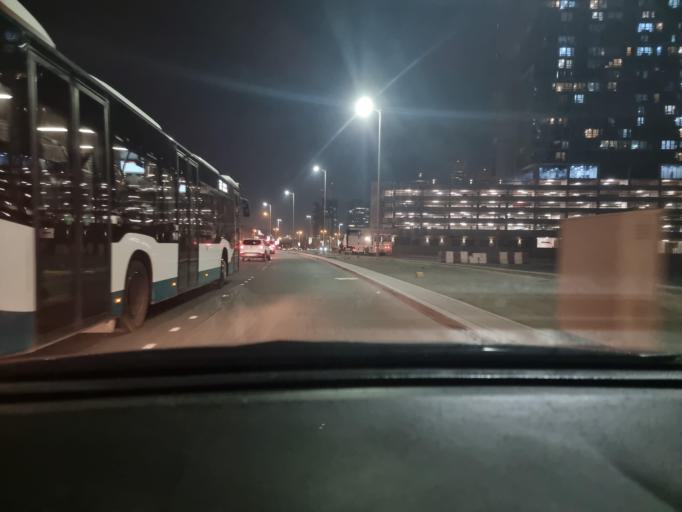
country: AE
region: Abu Dhabi
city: Abu Dhabi
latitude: 24.4943
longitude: 54.4058
